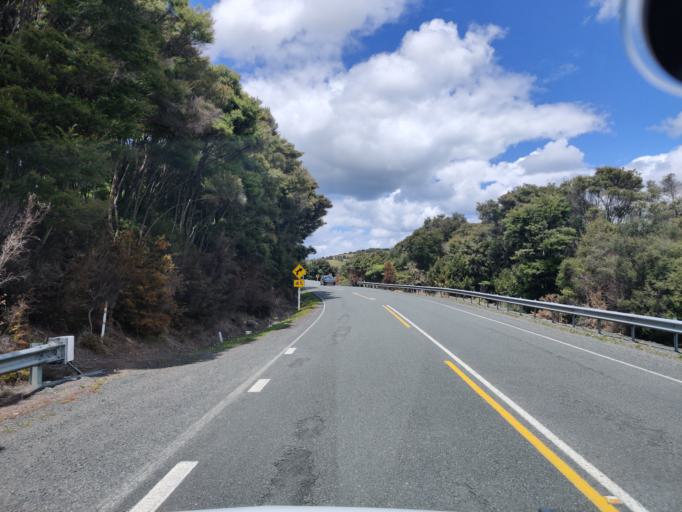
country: NZ
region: Northland
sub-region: Far North District
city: Paihia
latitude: -35.2862
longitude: 174.1482
